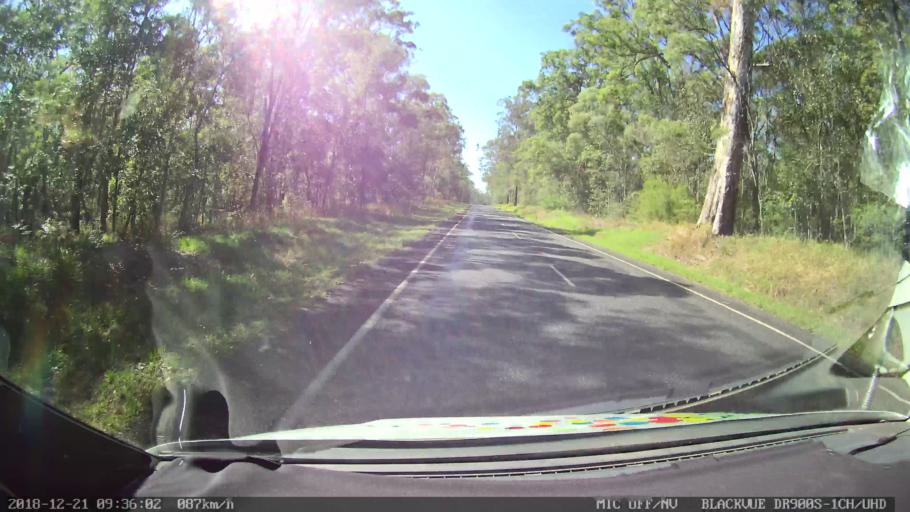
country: AU
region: New South Wales
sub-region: Clarence Valley
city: Grafton
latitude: -29.5182
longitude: 152.9815
